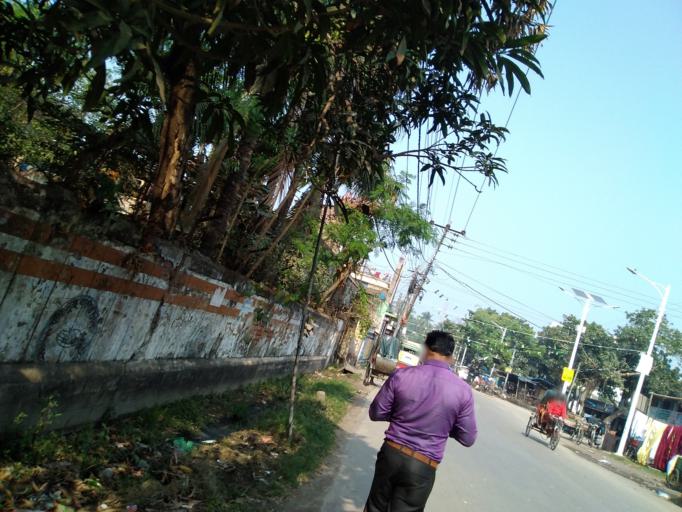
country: BD
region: Khulna
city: Khulna
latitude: 22.8069
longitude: 89.5772
